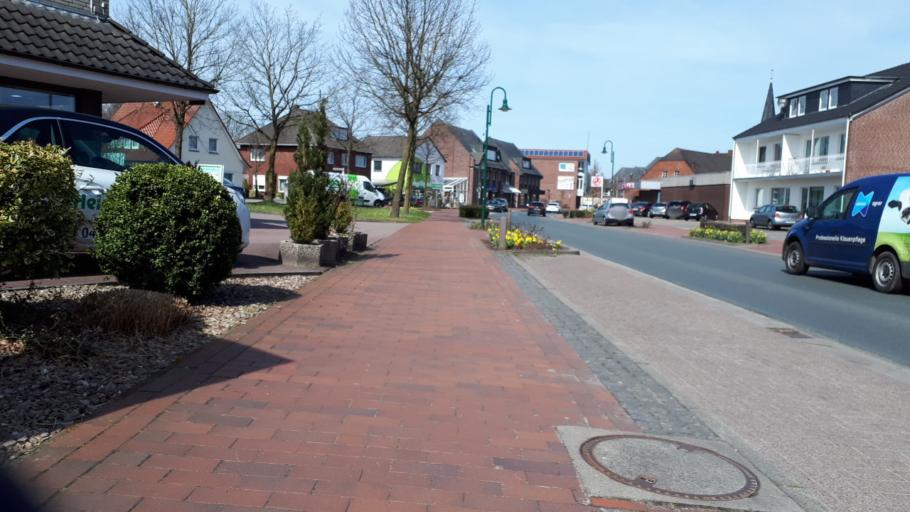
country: DE
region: Lower Saxony
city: Garrel
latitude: 52.9534
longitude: 8.0252
